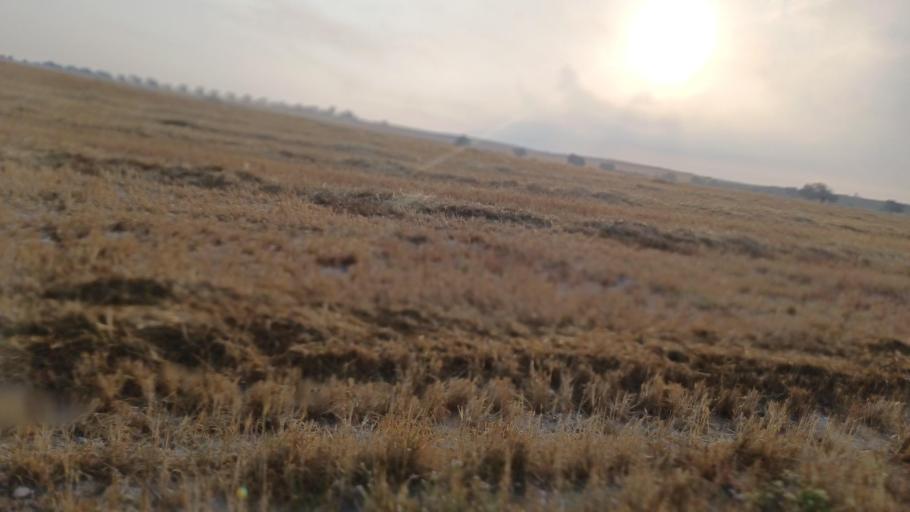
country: CY
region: Larnaka
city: Tersefanou
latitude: 34.8336
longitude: 33.5210
